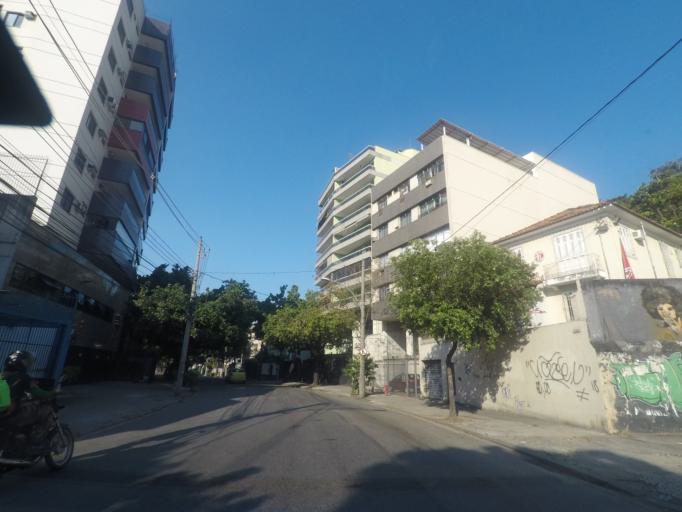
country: BR
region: Rio de Janeiro
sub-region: Rio De Janeiro
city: Rio de Janeiro
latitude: -22.9159
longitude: -43.2172
